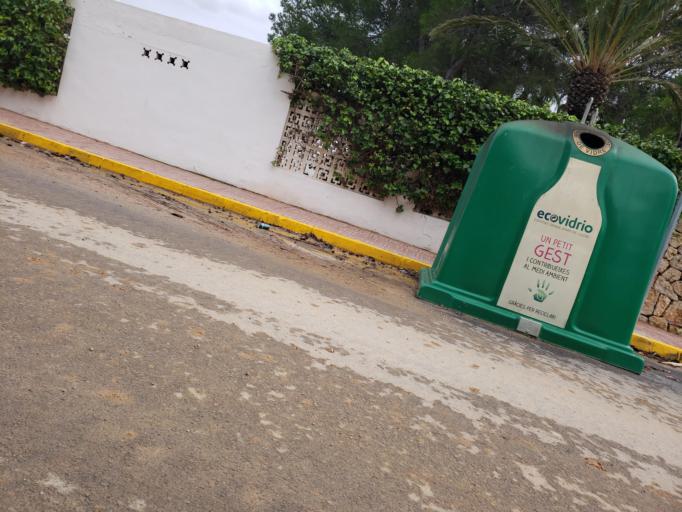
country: ES
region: Balearic Islands
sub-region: Illes Balears
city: Sant Joan de Labritja
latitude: 39.1101
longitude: 1.5096
